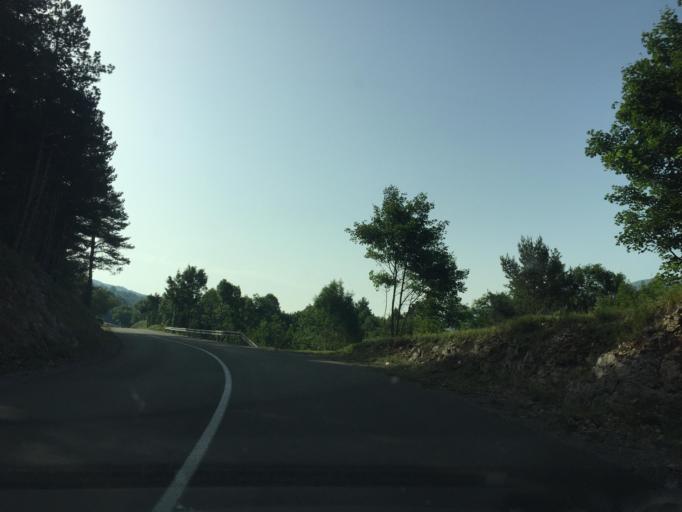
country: HR
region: Primorsko-Goranska
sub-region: Grad Opatija
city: Opatija
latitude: 45.4452
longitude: 14.1866
